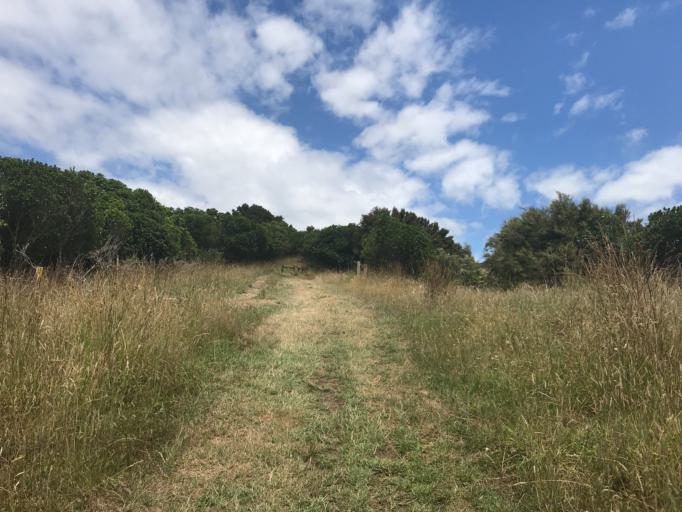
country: NZ
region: Marlborough
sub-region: Marlborough District
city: Picton
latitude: -41.2131
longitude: 173.9960
